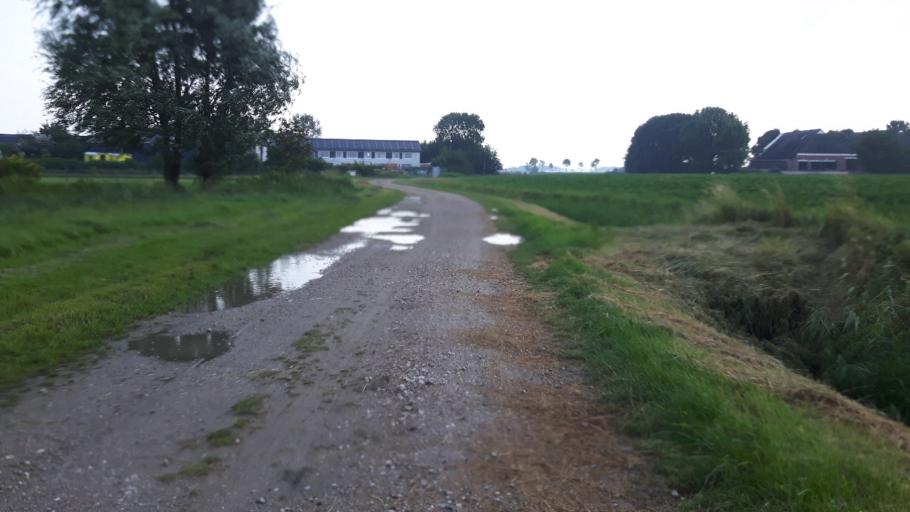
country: NL
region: Groningen
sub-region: Gemeente Appingedam
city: Appingedam
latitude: 53.3349
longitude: 6.7364
